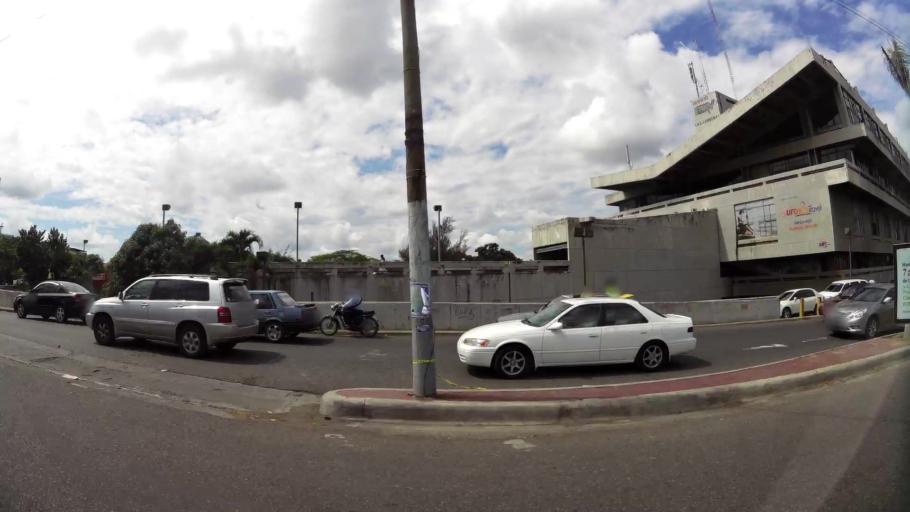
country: DO
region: Santiago
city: Santiago de los Caballeros
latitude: 19.4564
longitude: -70.7057
